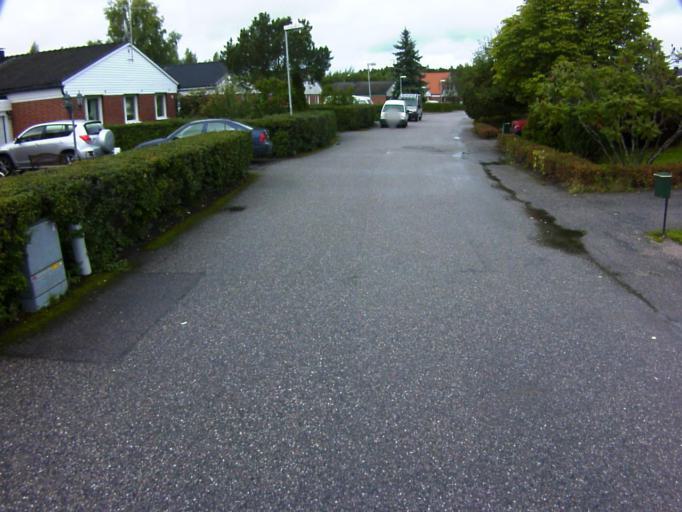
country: SE
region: Soedermanland
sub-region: Eskilstuna Kommun
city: Torshalla
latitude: 59.3770
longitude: 16.4656
